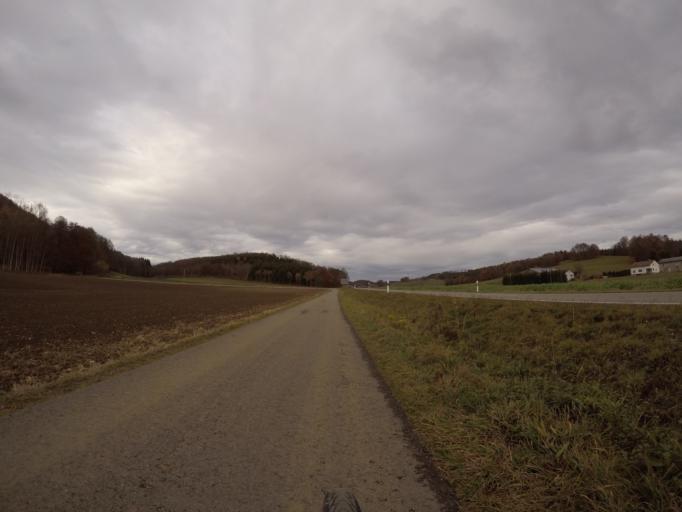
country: DE
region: Baden-Wuerttemberg
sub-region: Tuebingen Region
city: Sankt Johann
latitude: 48.4054
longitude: 9.2861
